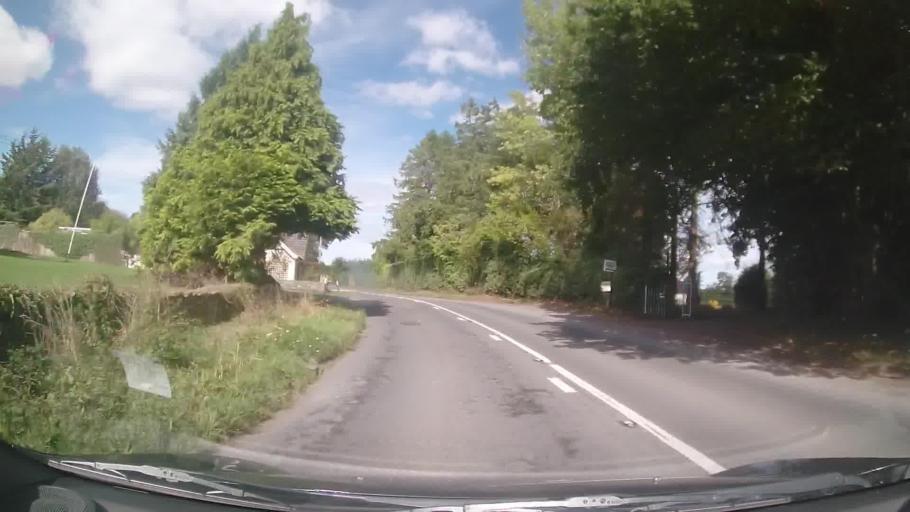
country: GB
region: England
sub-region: Herefordshire
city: Kinnersley
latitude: 52.1341
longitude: -3.0048
